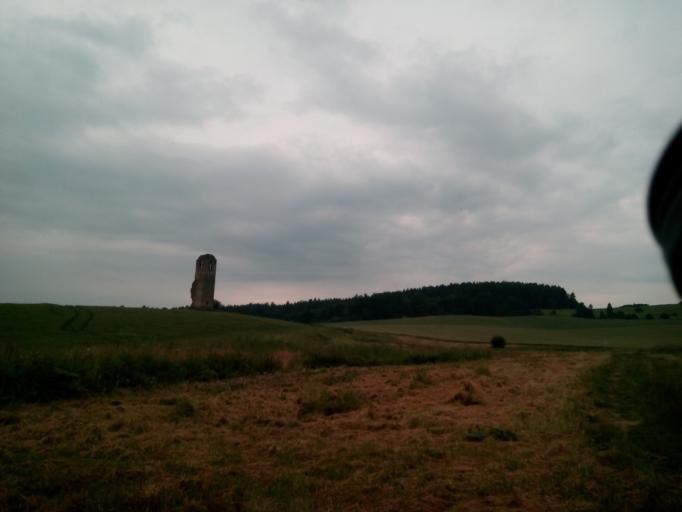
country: SK
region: Presovsky
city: Spisske Podhradie
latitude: 48.9443
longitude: 20.6915
